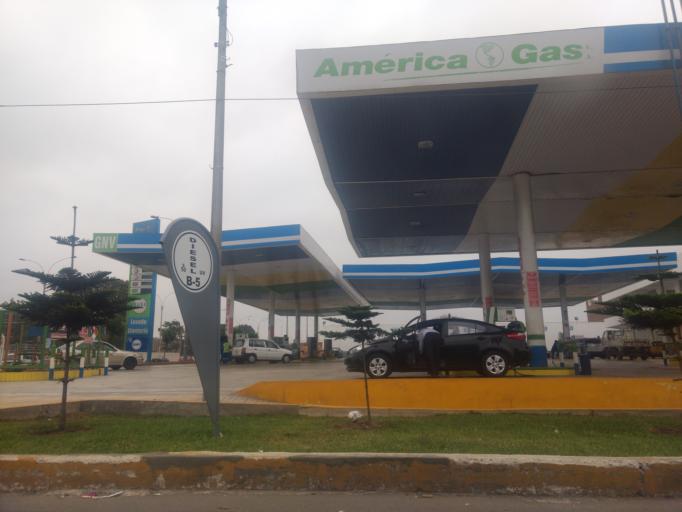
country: PE
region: Callao
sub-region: Callao
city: Callao
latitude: -12.0613
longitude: -77.0826
